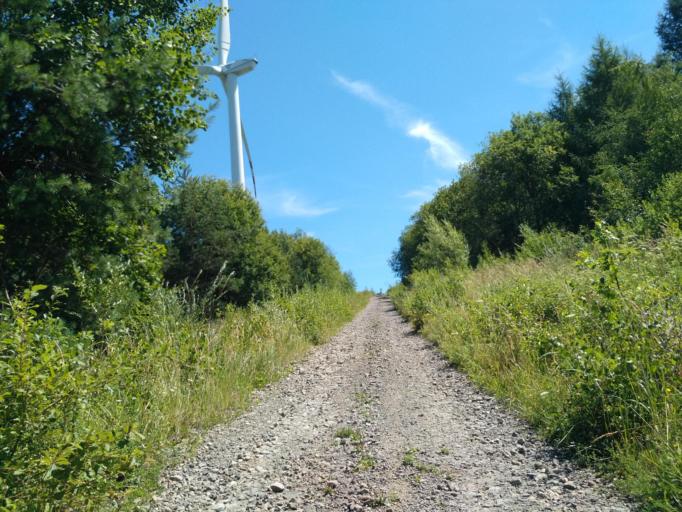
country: PL
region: Subcarpathian Voivodeship
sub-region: Powiat sanocki
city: Bukowsko
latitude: 49.4883
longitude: 22.0863
